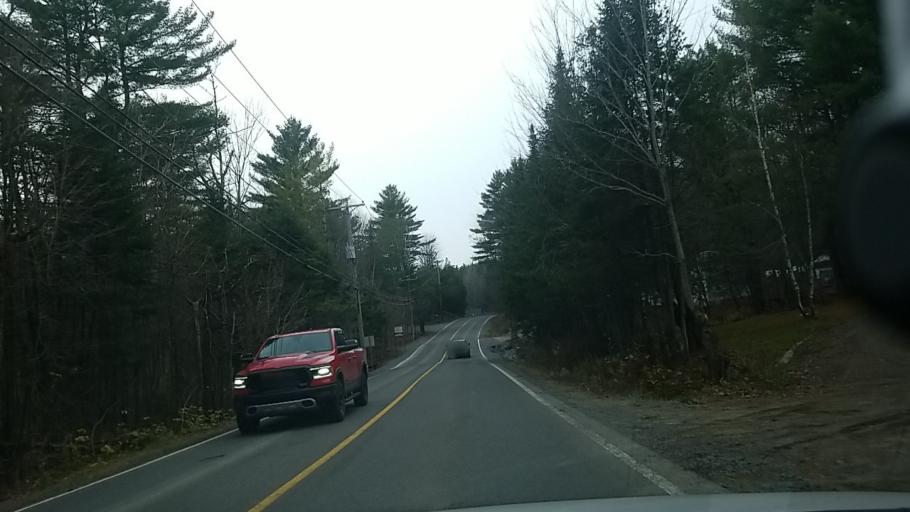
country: CA
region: Quebec
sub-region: Laurentides
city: Saint-Colomban
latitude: 45.7826
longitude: -74.1043
